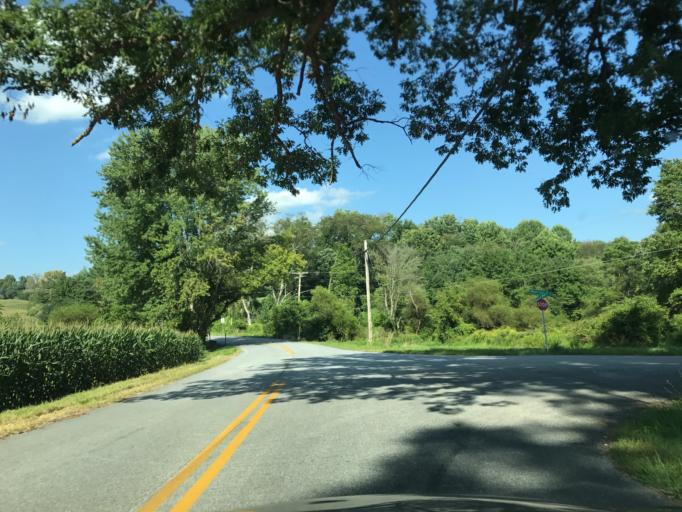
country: US
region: Pennsylvania
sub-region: York County
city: Stewartstown
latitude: 39.6931
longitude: -76.5857
